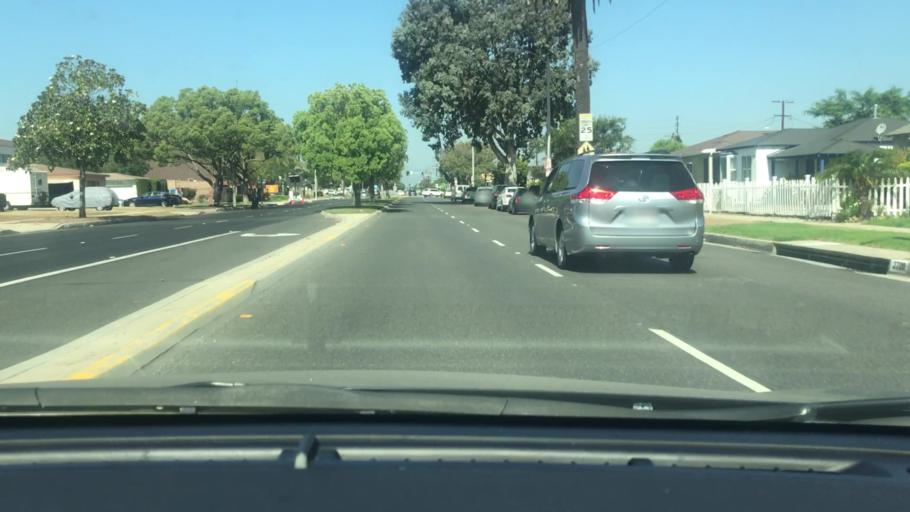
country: US
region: California
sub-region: Los Angeles County
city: Alondra Park
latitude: 33.8874
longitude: -118.3238
